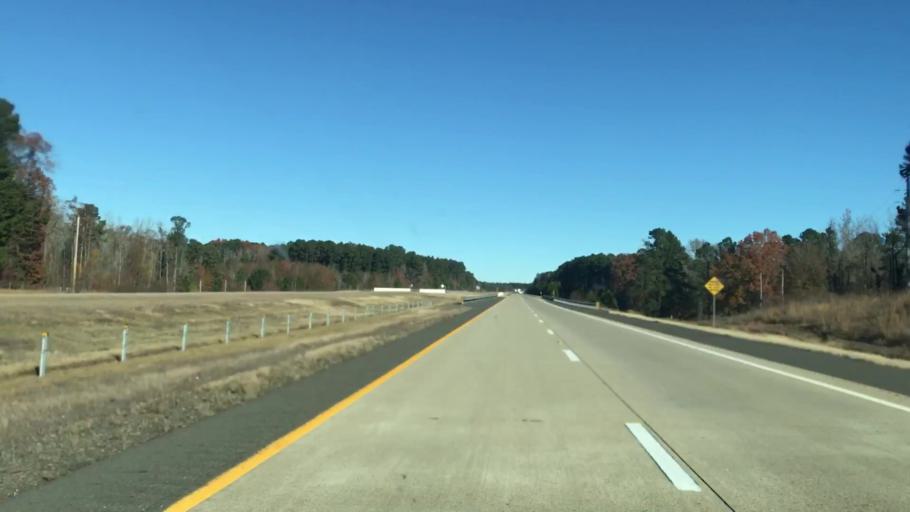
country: US
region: Louisiana
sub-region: Caddo Parish
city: Vivian
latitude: 33.0901
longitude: -93.8946
